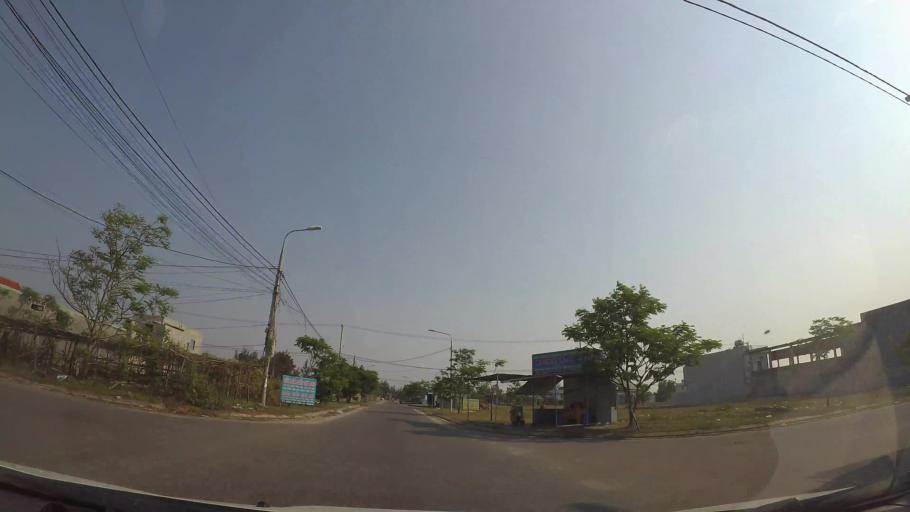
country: VN
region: Quang Nam
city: Quang Nam
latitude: 15.9522
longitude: 108.2599
